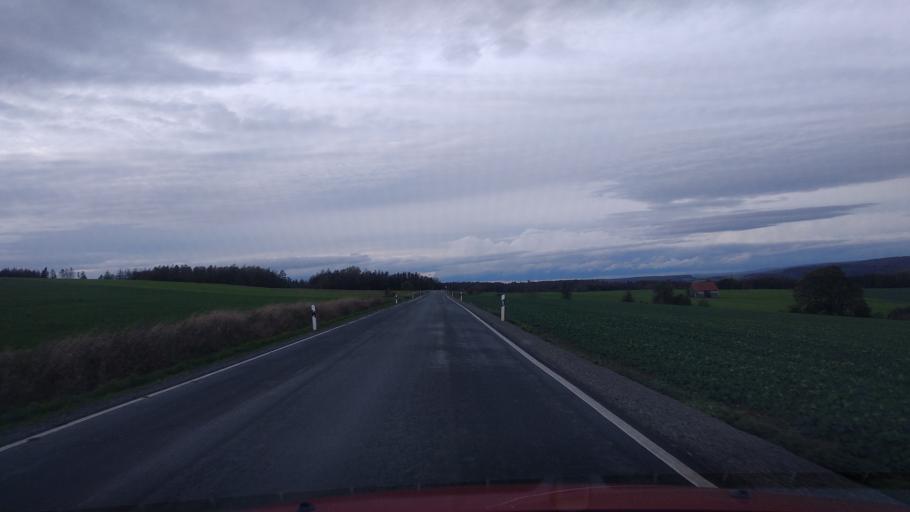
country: DE
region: North Rhine-Westphalia
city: Brakel
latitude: 51.6634
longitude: 9.2665
